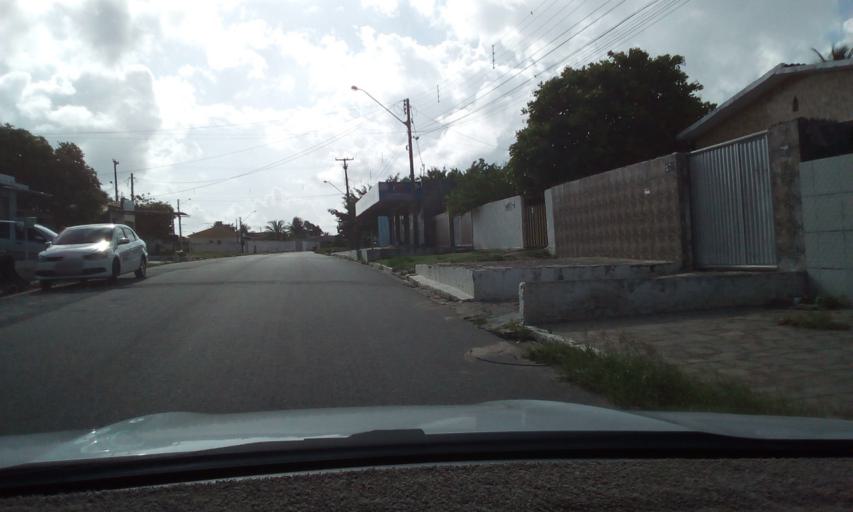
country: BR
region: Paraiba
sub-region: Joao Pessoa
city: Joao Pessoa
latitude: -7.1824
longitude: -34.8279
